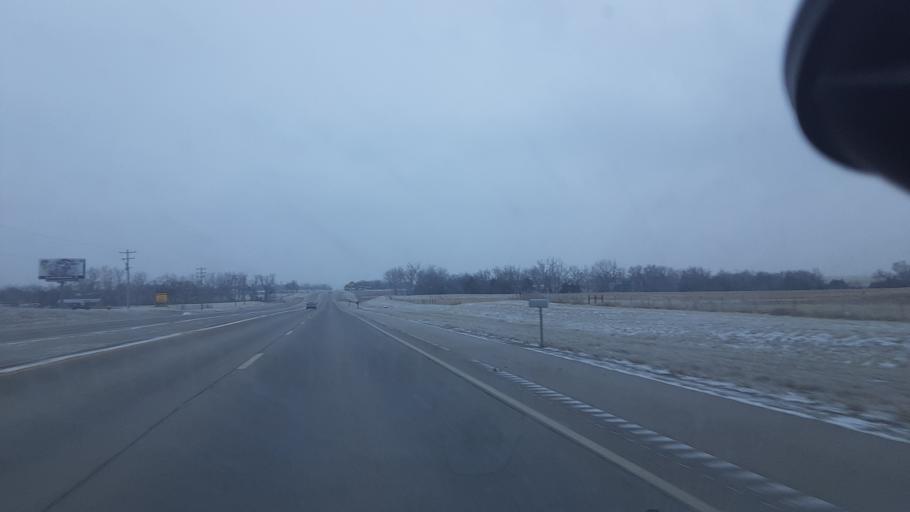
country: US
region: Oklahoma
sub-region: Payne County
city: Perkins
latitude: 35.9854
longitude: -97.0770
